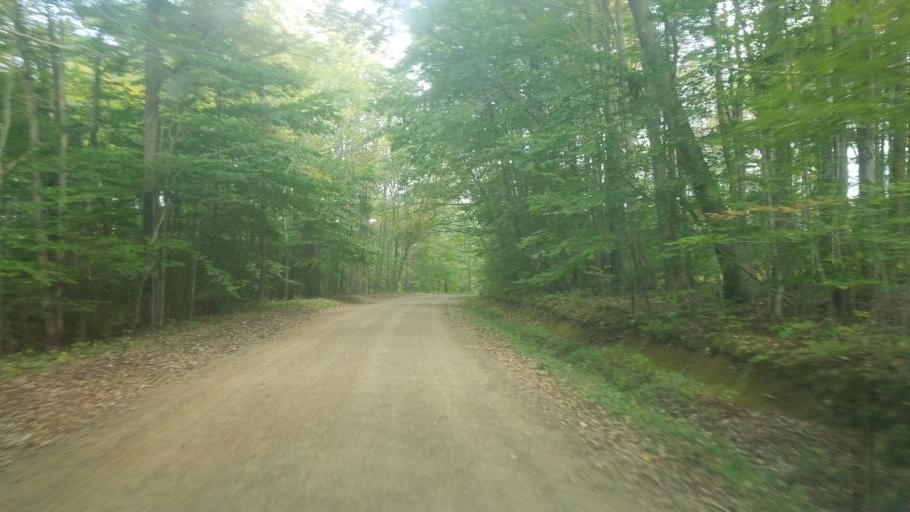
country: US
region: New York
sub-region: Allegany County
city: Cuba
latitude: 42.1416
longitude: -78.3022
